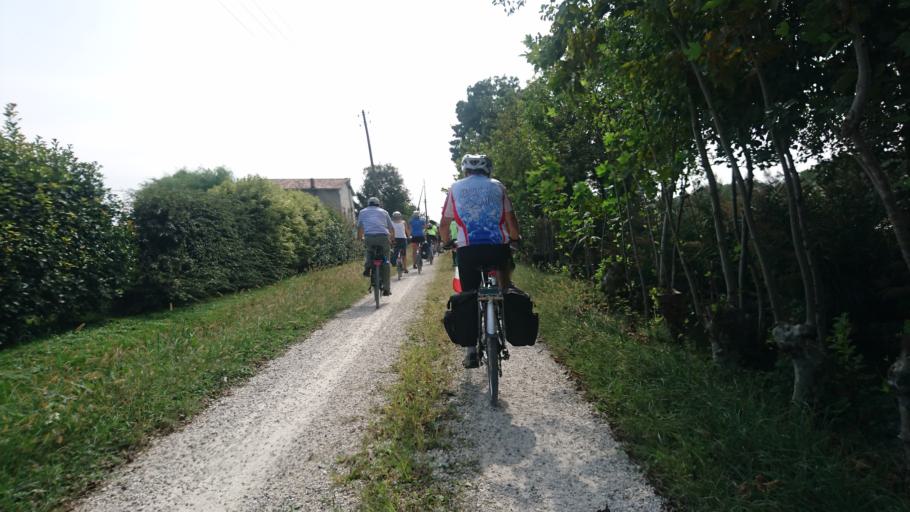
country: IT
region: Veneto
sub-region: Provincia di Padova
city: San Giorgio in Bosco
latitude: 45.5837
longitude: 11.7708
